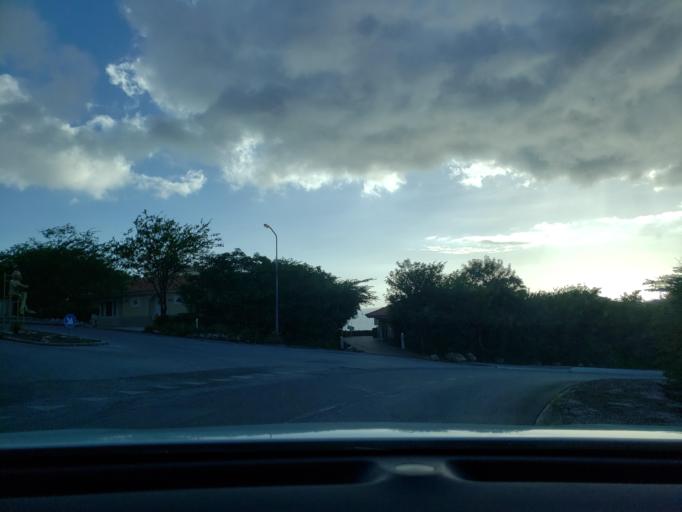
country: CW
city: Dorp Soto
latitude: 12.2045
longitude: -69.0789
